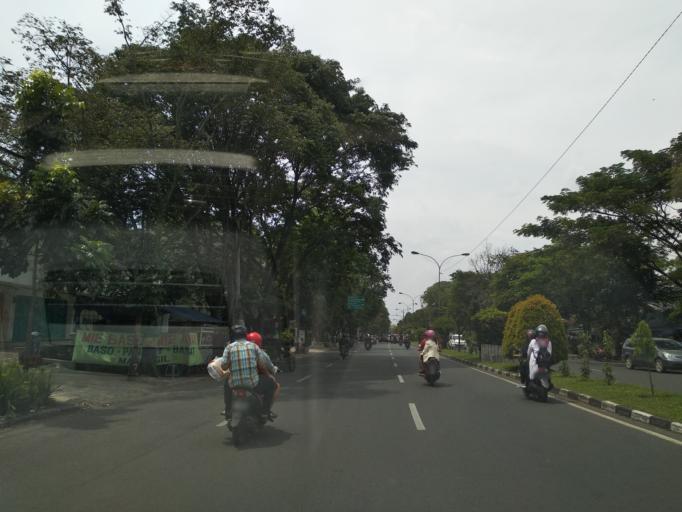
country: ID
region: West Java
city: Bandung
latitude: -6.9377
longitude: 107.6115
